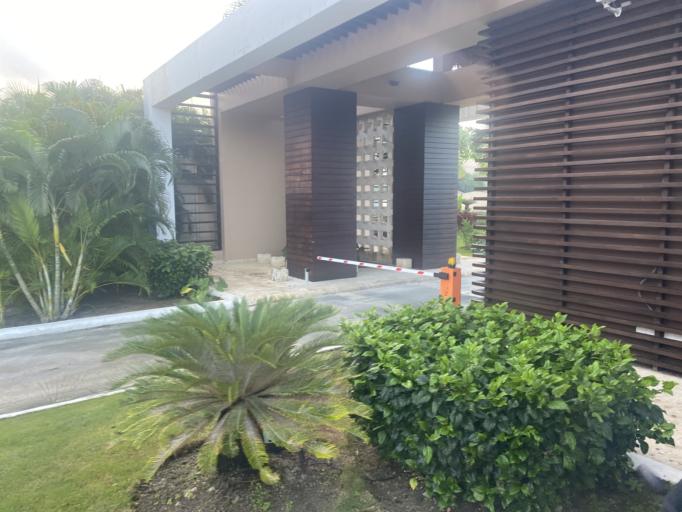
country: DO
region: San Juan
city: Punta Cana
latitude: 18.7257
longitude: -68.4716
